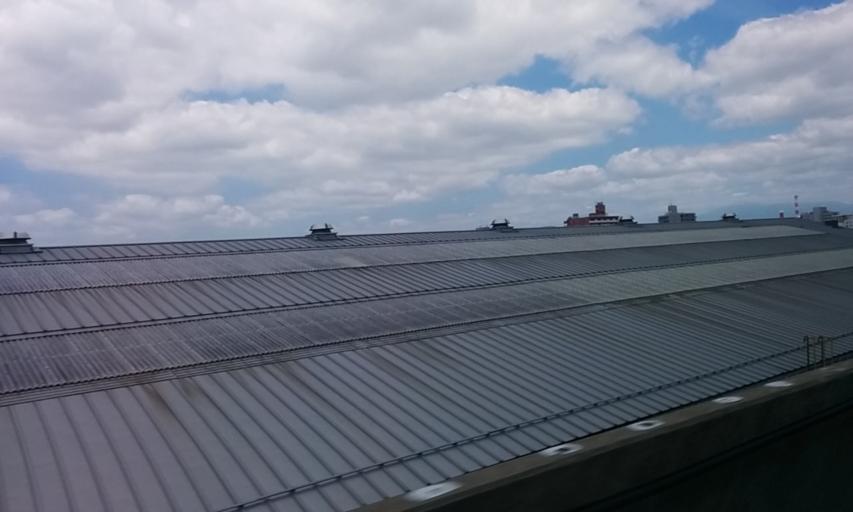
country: JP
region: Fukushima
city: Koriyama
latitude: 37.3860
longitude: 140.3857
